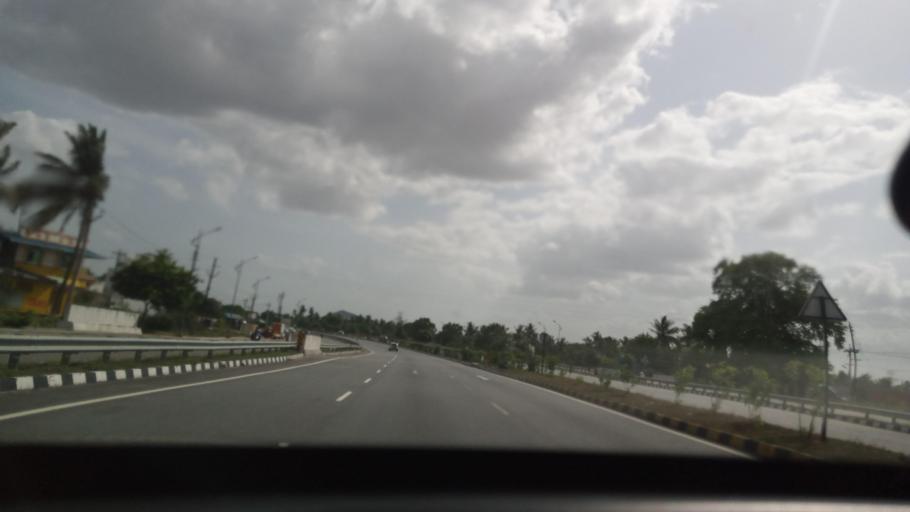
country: IN
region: Tamil Nadu
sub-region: Vellore
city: Jolarpettai
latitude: 12.5852
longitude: 78.5041
